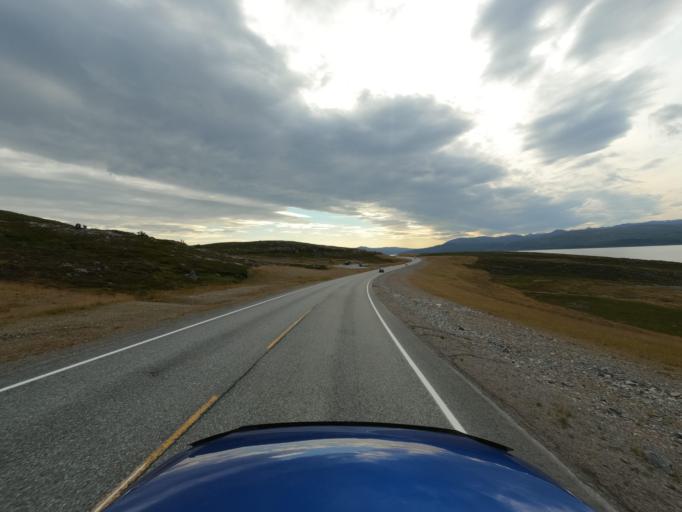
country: NO
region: Finnmark Fylke
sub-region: Hammerfest
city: Rypefjord
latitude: 70.5294
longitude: 23.7444
